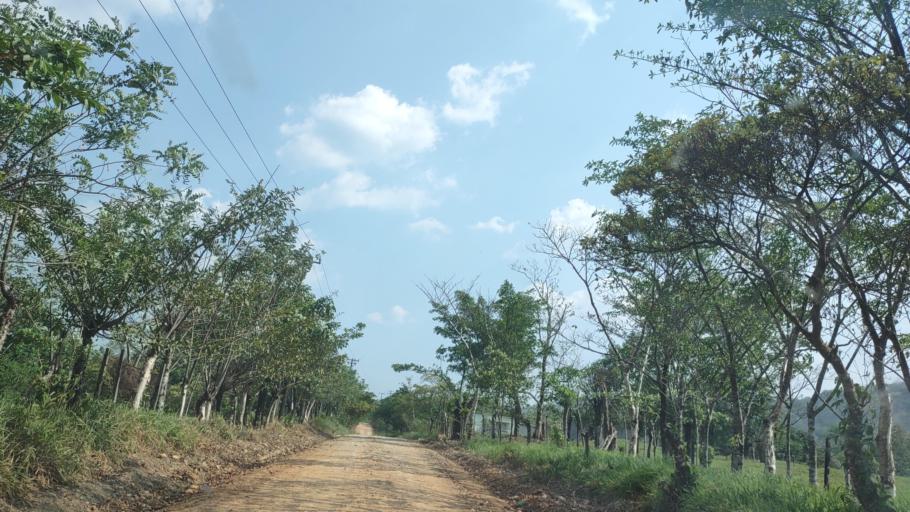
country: MX
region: Chiapas
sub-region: Tecpatan
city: Raudales Malpaso
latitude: 17.3457
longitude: -93.7555
